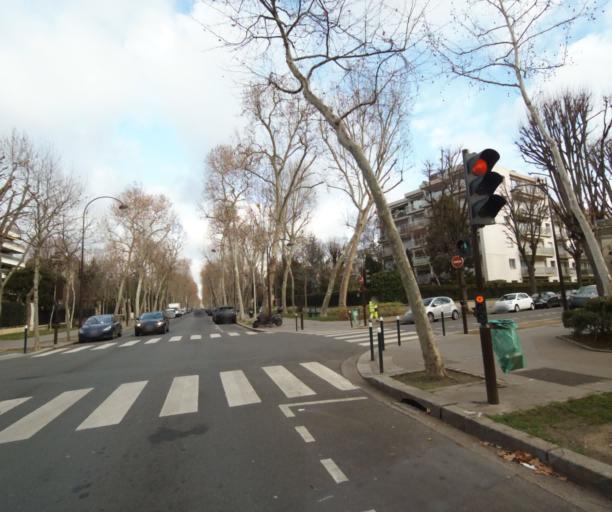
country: FR
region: Ile-de-France
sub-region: Departement des Hauts-de-Seine
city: Neuilly-sur-Seine
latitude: 48.8890
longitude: 2.2665
